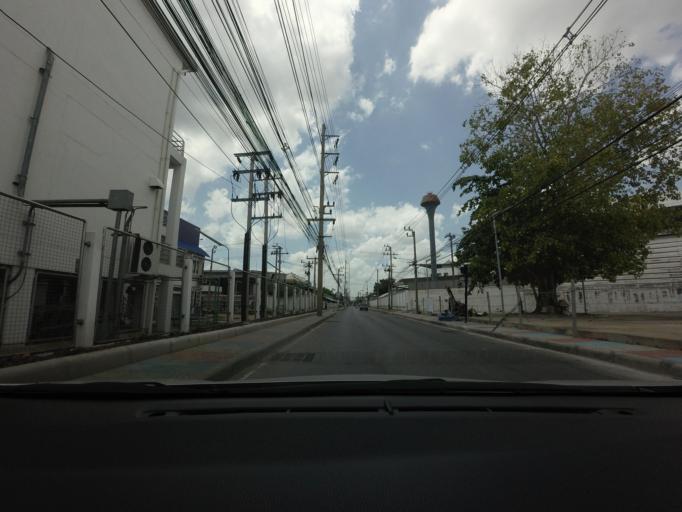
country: TH
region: Samut Prakan
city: Phra Samut Chedi
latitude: 13.6399
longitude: 100.5767
